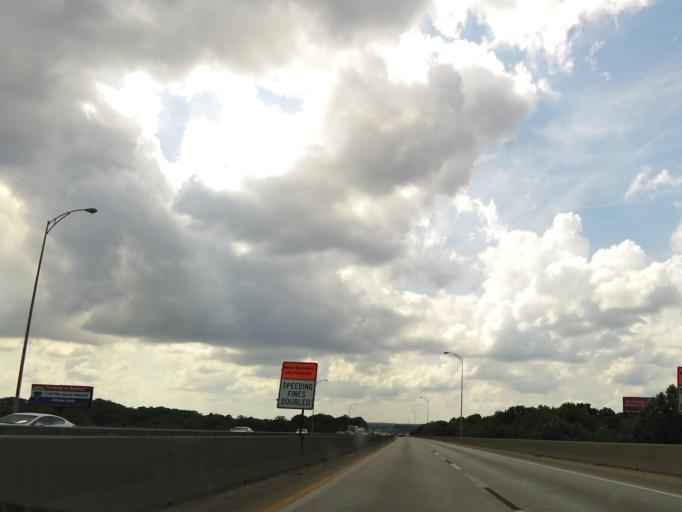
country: US
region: Alabama
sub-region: Jefferson County
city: Irondale
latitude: 33.5386
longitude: -86.7286
